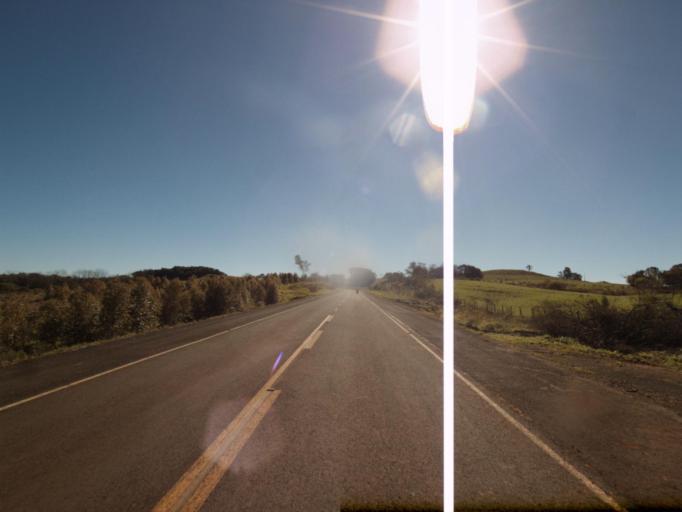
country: AR
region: Misiones
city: Bernardo de Irigoyen
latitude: -26.6123
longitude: -53.6880
